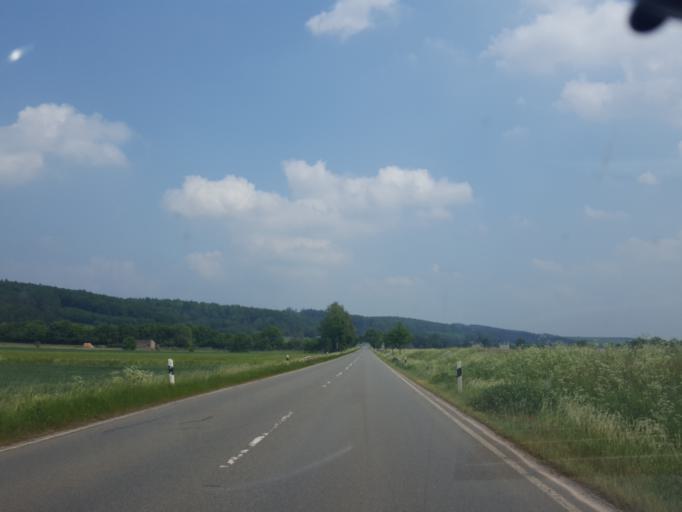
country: DE
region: Lower Saxony
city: Wulften
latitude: 51.6392
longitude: 10.1700
